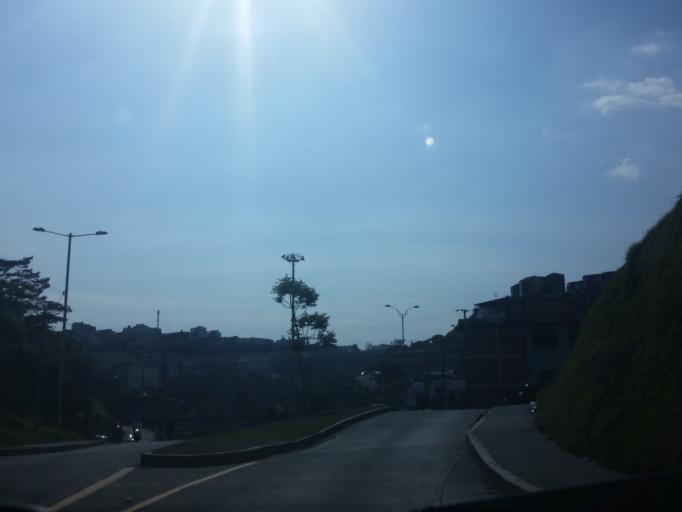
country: CO
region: Caldas
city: Manizales
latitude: 5.0725
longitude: -75.4932
